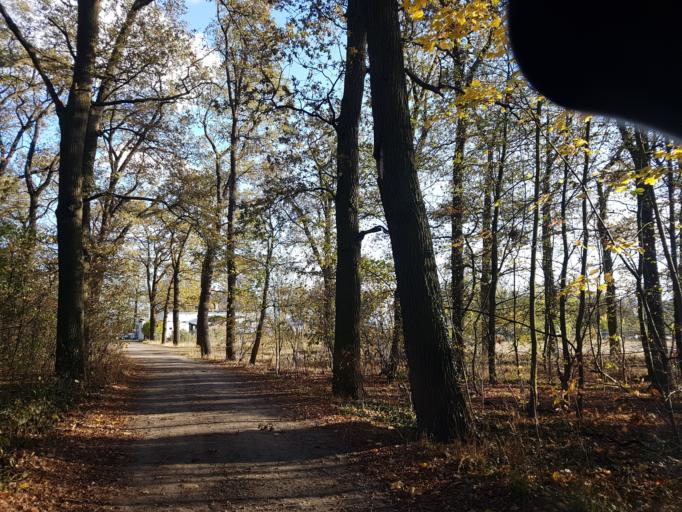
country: DE
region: Brandenburg
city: Nauen
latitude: 52.6316
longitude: 12.9019
